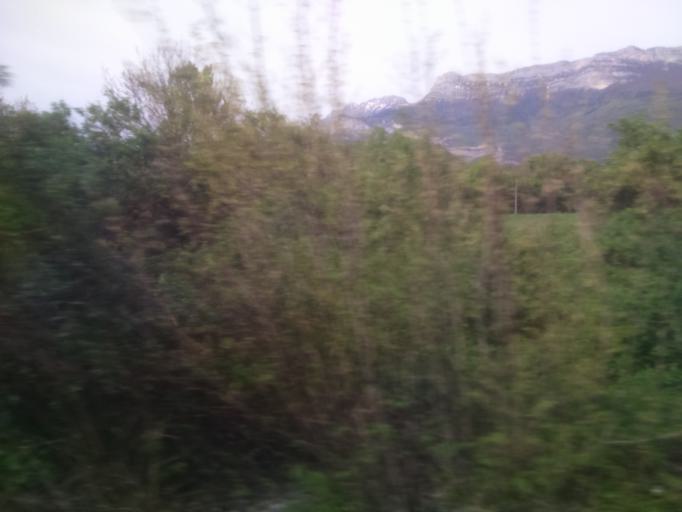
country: FR
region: Rhone-Alpes
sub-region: Departement de l'Isere
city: Le Pont-de-Claix
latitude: 45.1183
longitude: 5.7039
